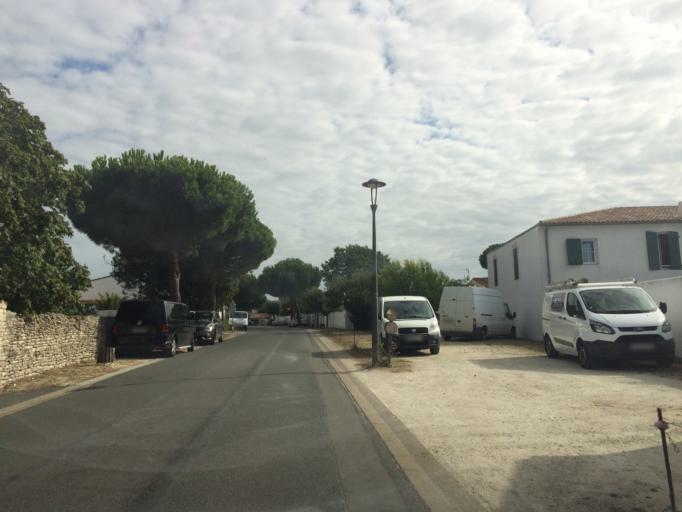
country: FR
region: Poitou-Charentes
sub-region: Departement de la Charente-Maritime
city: La Flotte
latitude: 46.1892
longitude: -1.3341
